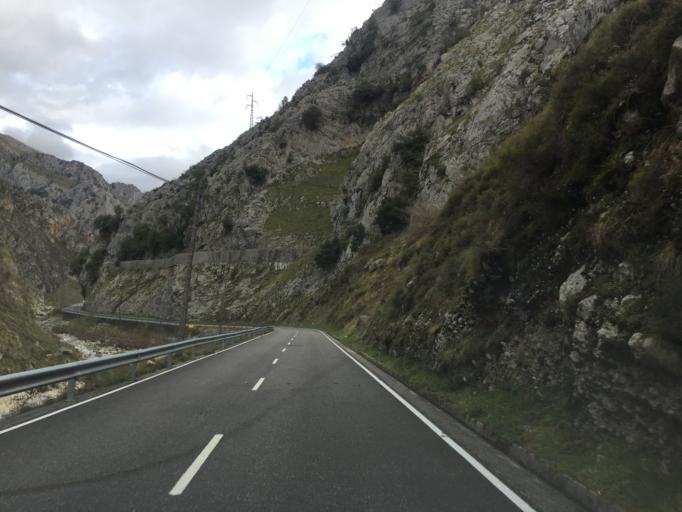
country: ES
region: Asturias
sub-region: Province of Asturias
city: Carrena
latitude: 43.2690
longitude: -4.8310
